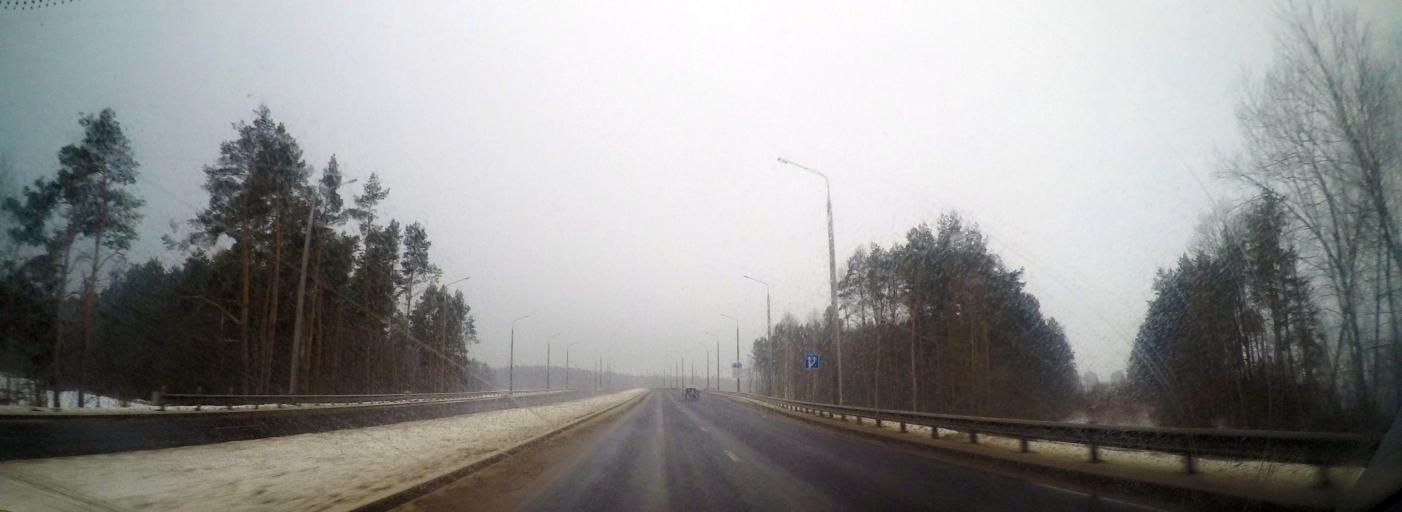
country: BY
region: Grodnenskaya
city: Hrodna
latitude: 53.6413
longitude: 23.8818
